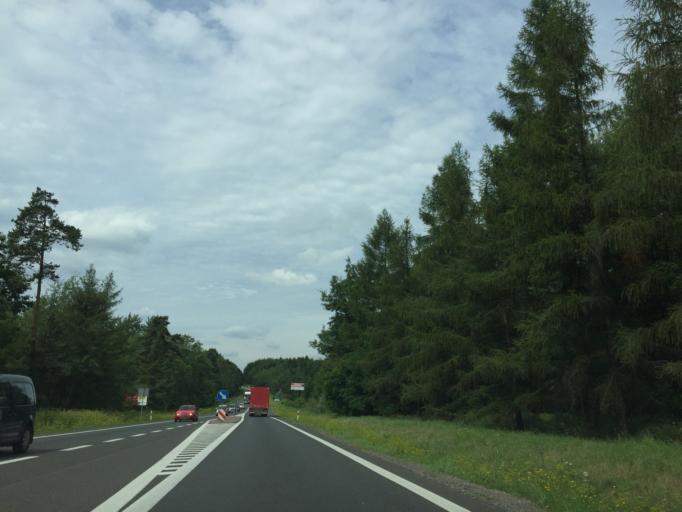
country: PL
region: Lesser Poland Voivodeship
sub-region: Powiat olkuski
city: Osiek
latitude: 50.2684
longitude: 19.6062
